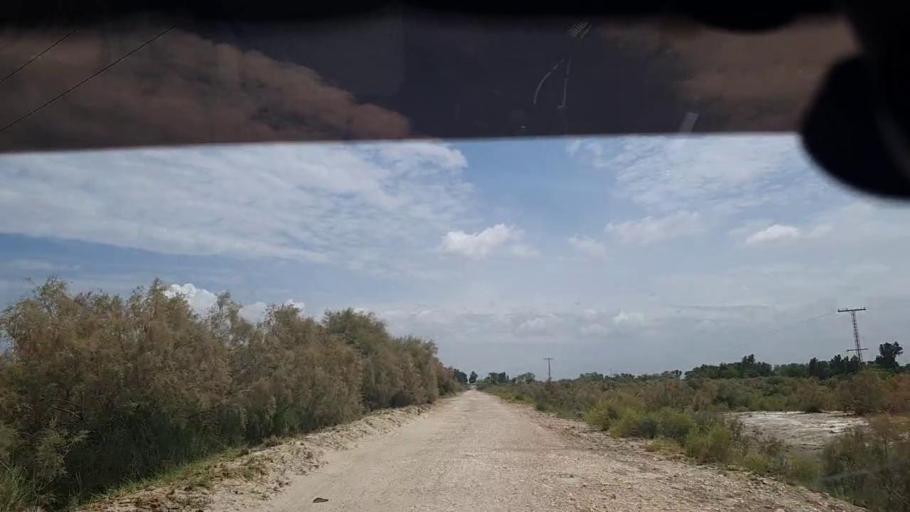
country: PK
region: Sindh
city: Rustam jo Goth
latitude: 28.0251
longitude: 68.9391
